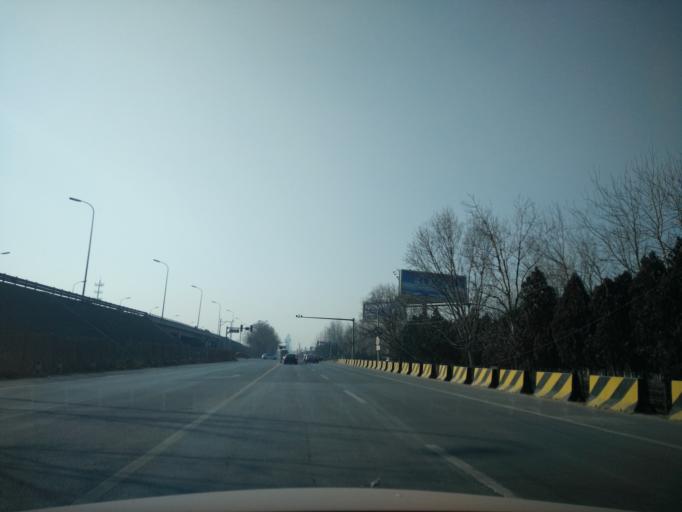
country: CN
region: Beijing
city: Jiugong
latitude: 39.8147
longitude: 116.4873
